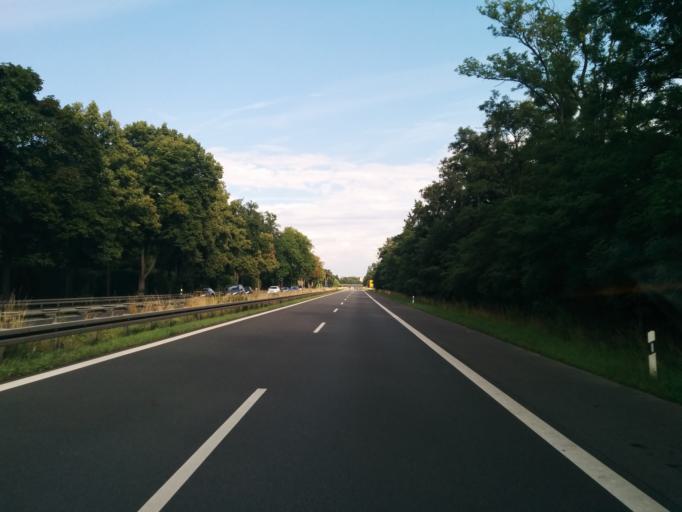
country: DE
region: Brandenburg
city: Wustermark
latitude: 52.5363
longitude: 12.9881
